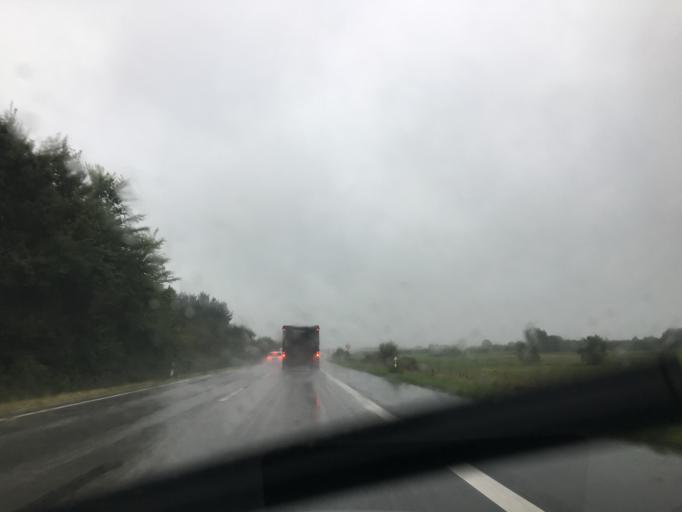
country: DE
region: Schleswig-Holstein
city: Schonbek
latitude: 54.1590
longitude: 9.9621
